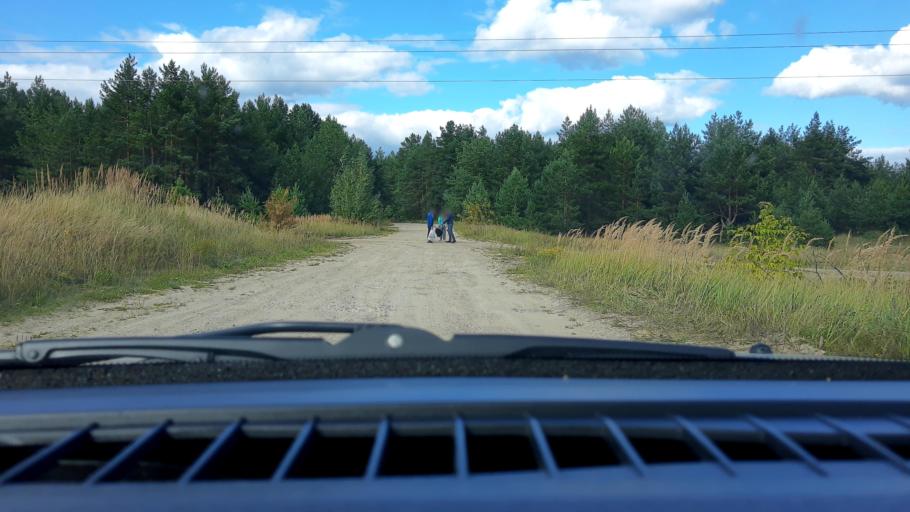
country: RU
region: Nizjnij Novgorod
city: Lukino
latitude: 56.3855
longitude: 43.7088
